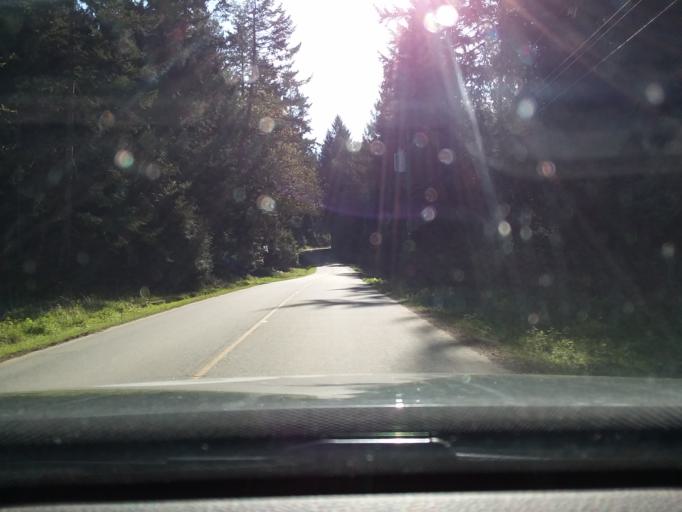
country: CA
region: British Columbia
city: North Cowichan
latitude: 48.9477
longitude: -123.5159
